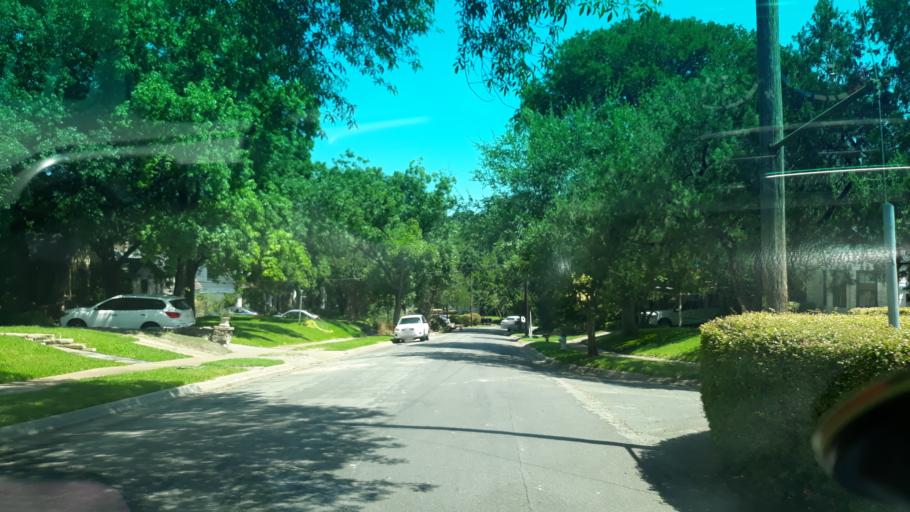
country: US
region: Texas
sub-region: Dallas County
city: Highland Park
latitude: 32.8172
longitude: -96.7397
